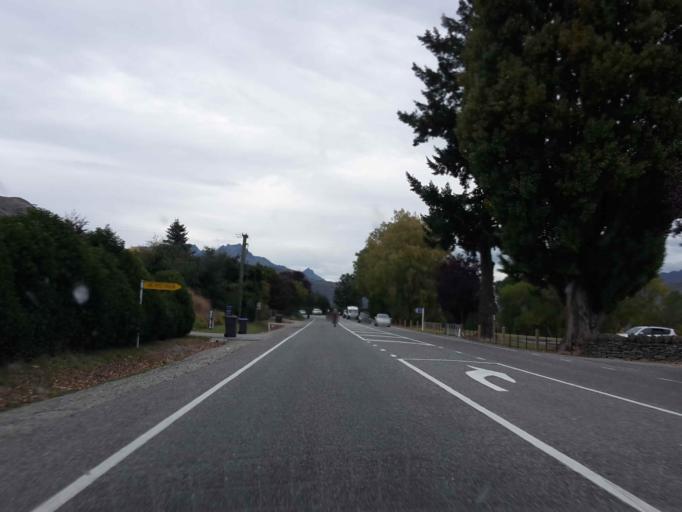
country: NZ
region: Otago
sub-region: Queenstown-Lakes District
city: Arrowtown
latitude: -44.9902
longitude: 168.8104
